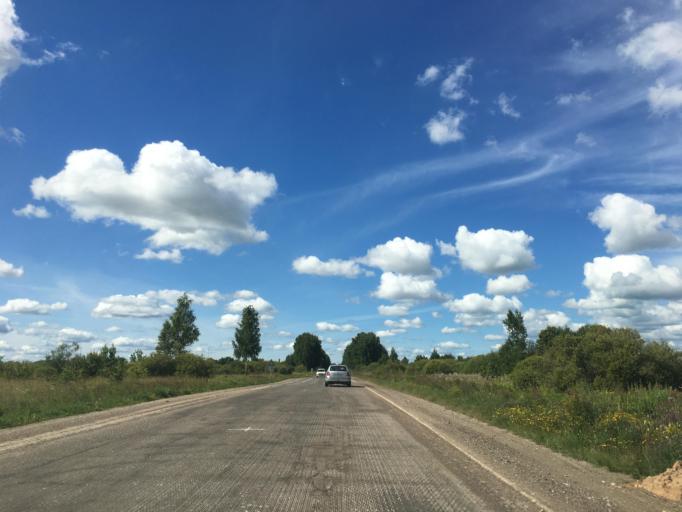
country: RU
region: Pskov
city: Palkino
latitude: 57.5476
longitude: 28.0358
